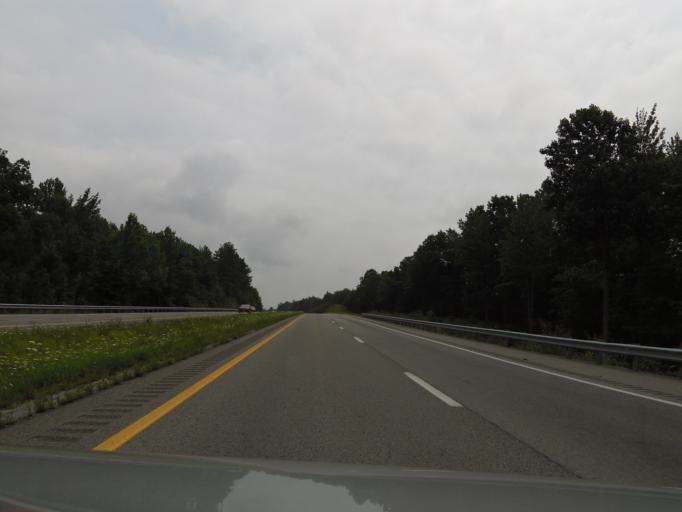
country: US
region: Kentucky
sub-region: Muhlenberg County
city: Central City
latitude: 37.3167
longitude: -87.0457
